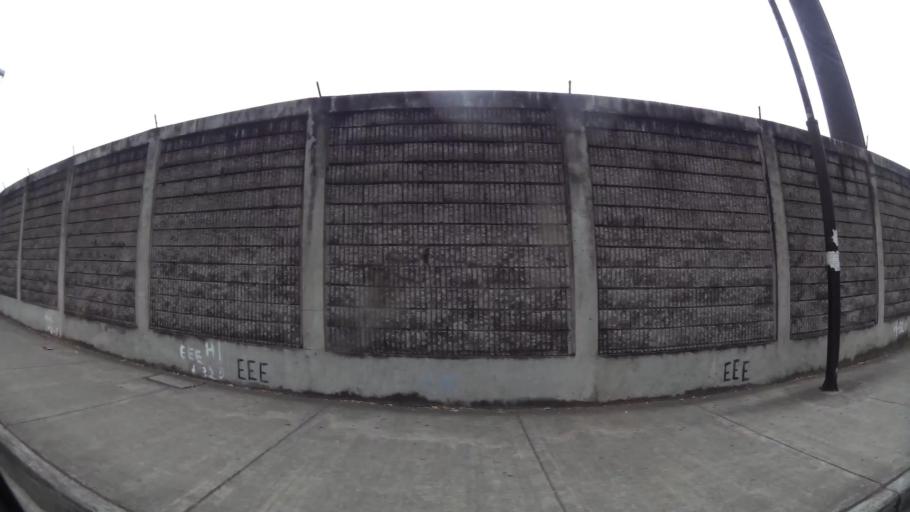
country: EC
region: Guayas
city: Eloy Alfaro
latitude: -2.1703
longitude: -79.8801
